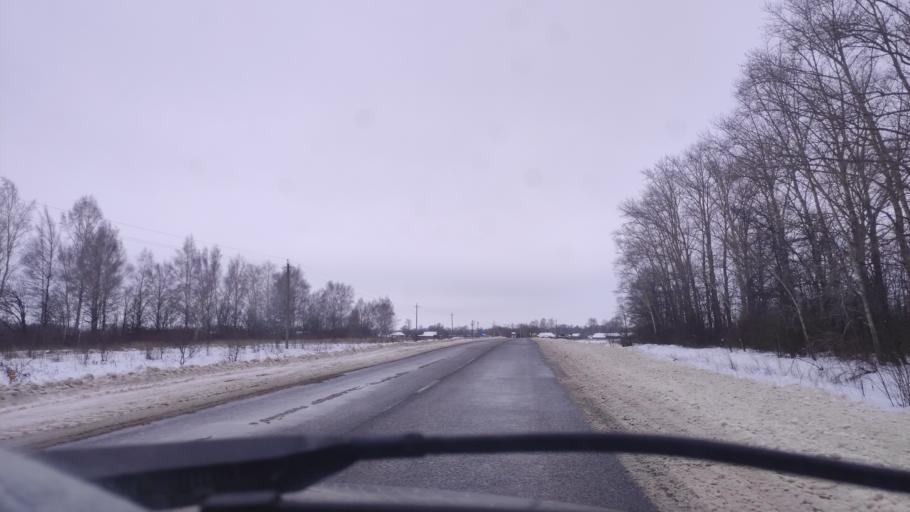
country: RU
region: Tambov
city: Pervomayskiy
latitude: 53.3056
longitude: 40.3877
